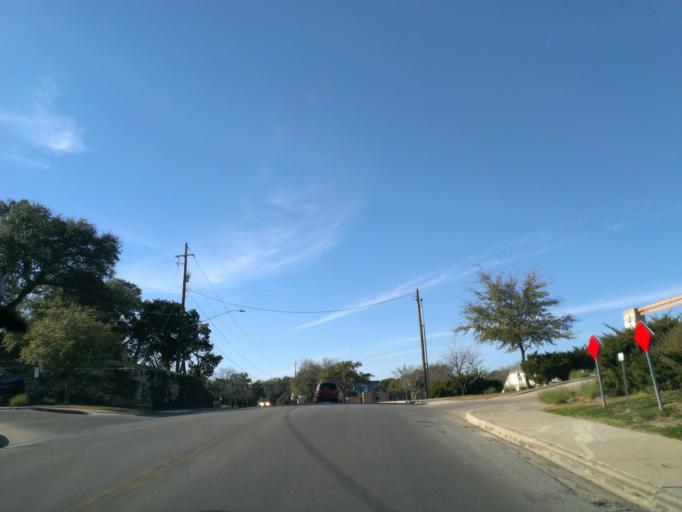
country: US
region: Texas
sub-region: Travis County
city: Austin
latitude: 30.2360
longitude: -97.7528
